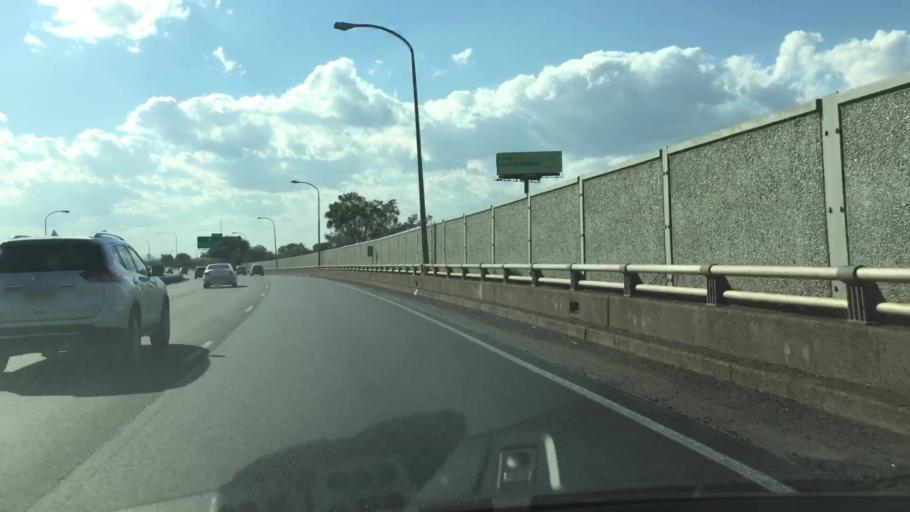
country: US
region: New Jersey
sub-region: Burlington County
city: Palmyra
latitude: 40.0085
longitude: -75.0688
